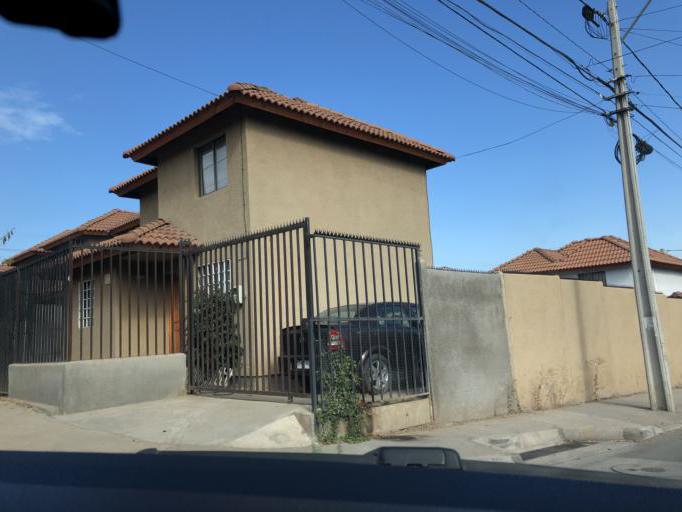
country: CL
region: Santiago Metropolitan
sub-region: Provincia de Cordillera
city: Puente Alto
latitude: -33.5764
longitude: -70.5404
